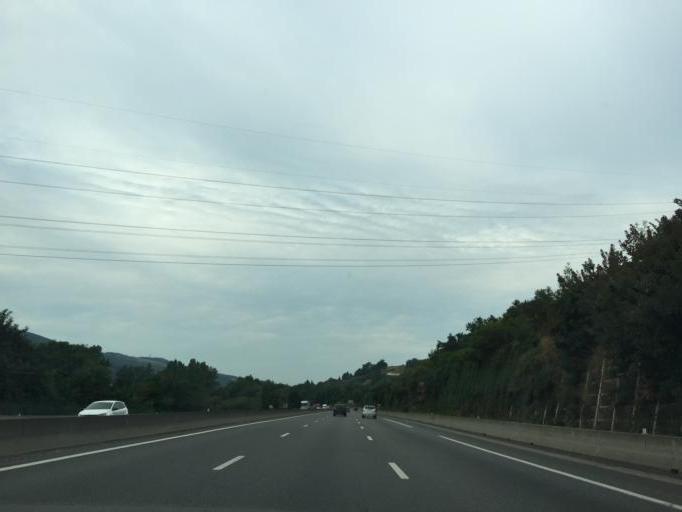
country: FR
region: Rhone-Alpes
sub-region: Departement de la Loire
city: Saint-Jean-Bonnefonds
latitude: 45.4491
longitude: 4.4719
